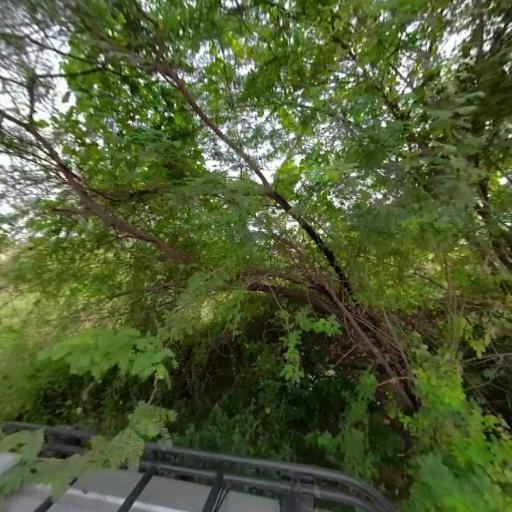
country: IN
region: Telangana
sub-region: Nalgonda
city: Suriapet
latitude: 17.2060
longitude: 79.4883
